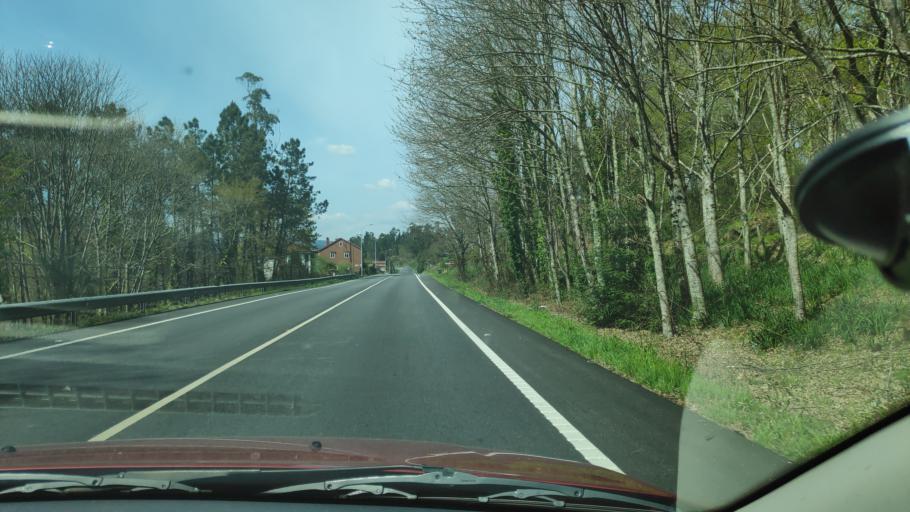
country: ES
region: Galicia
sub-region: Provincia da Coruna
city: Ames
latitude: 42.8874
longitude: -8.6845
